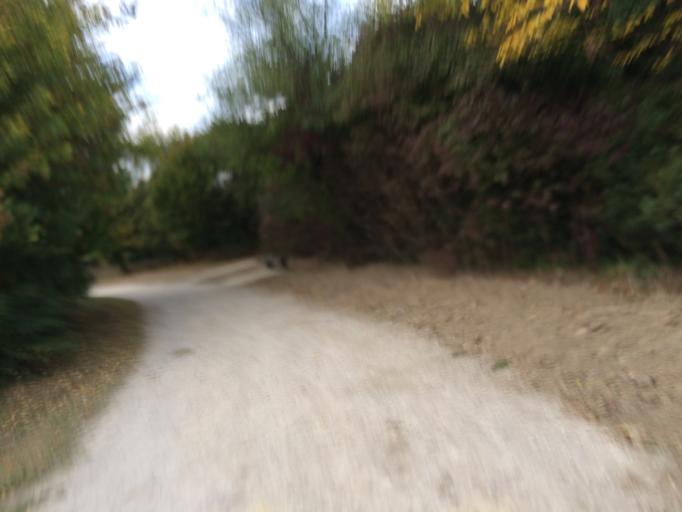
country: FR
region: Ile-de-France
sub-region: Departement de l'Essonne
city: Linas
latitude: 48.6367
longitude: 2.2605
